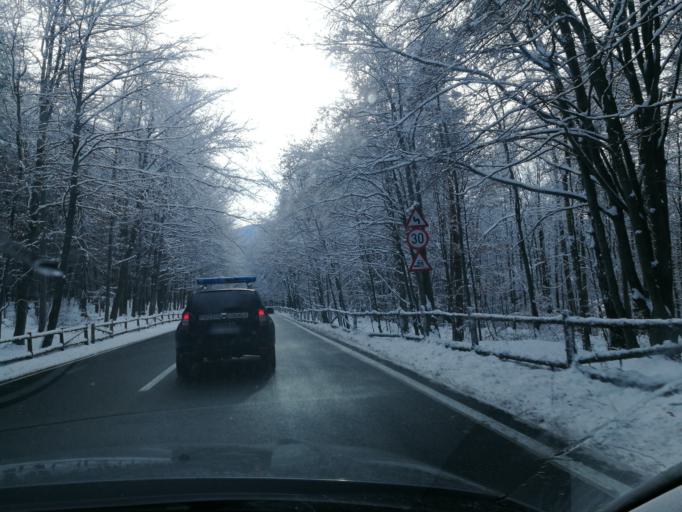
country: RO
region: Brasov
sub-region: Comuna Ghimbav
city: Ghimbav
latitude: 45.6186
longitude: 25.5439
